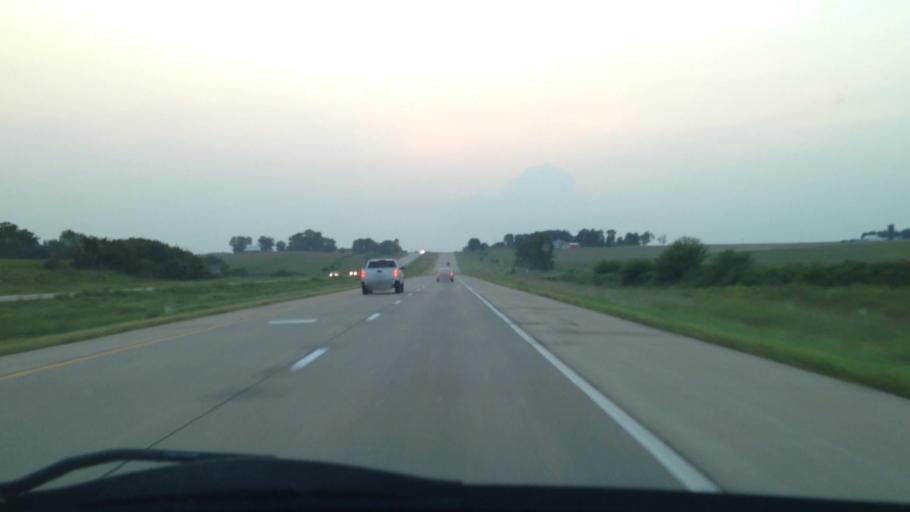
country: US
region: Iowa
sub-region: Buchanan County
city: Jesup
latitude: 42.3360
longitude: -92.0165
